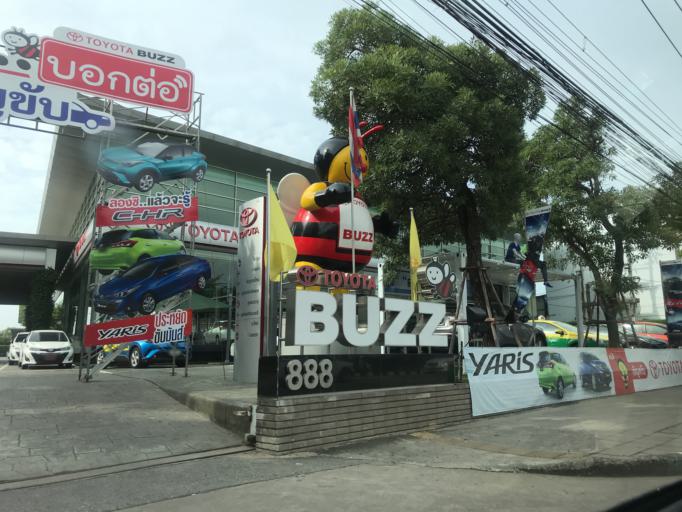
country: TH
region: Bangkok
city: Bueng Kum
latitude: 13.7861
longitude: 100.6760
